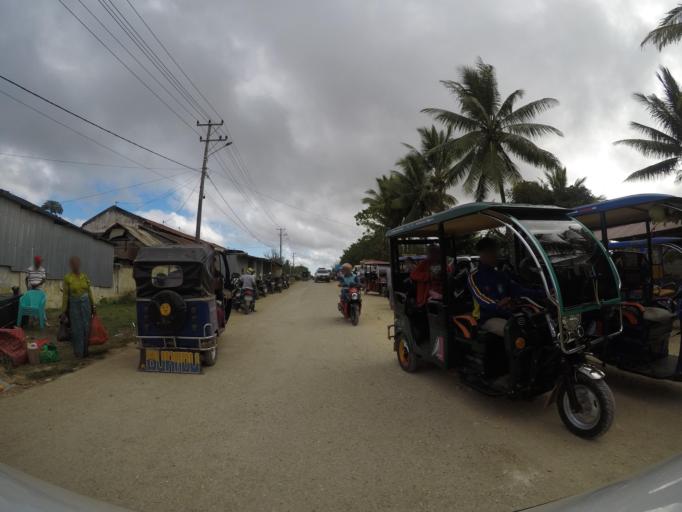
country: TL
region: Lautem
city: Lospalos
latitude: -8.5118
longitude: 127.0044
